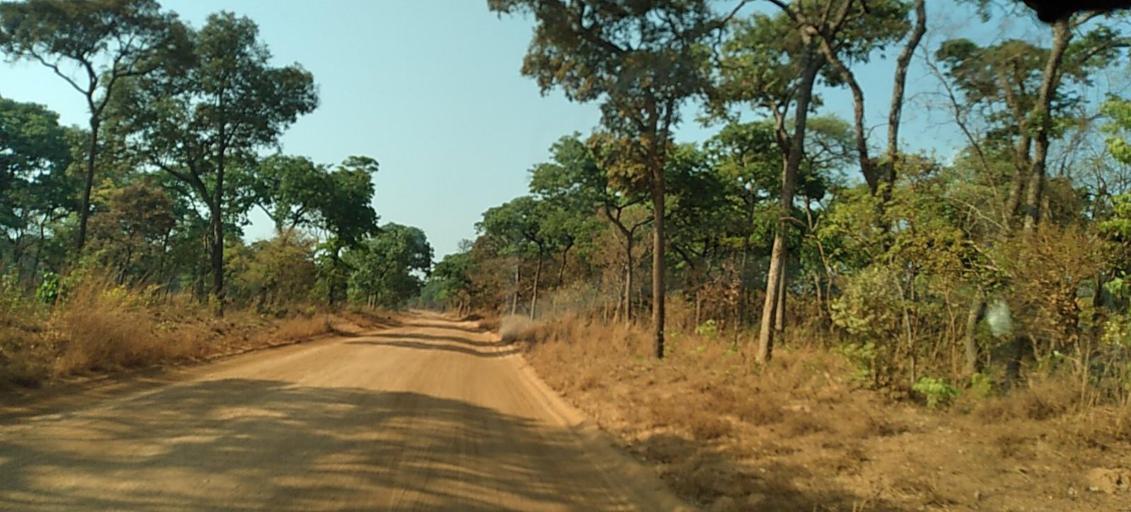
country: ZM
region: North-Western
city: Kasempa
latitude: -13.6588
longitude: 26.0093
